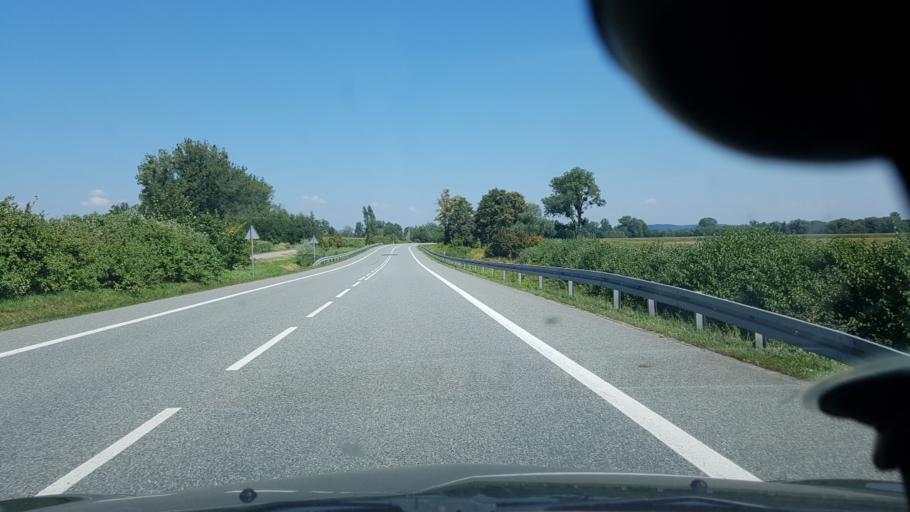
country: PL
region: Silesian Voivodeship
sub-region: Powiat raciborski
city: Chalupki
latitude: 49.9318
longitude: 18.3247
